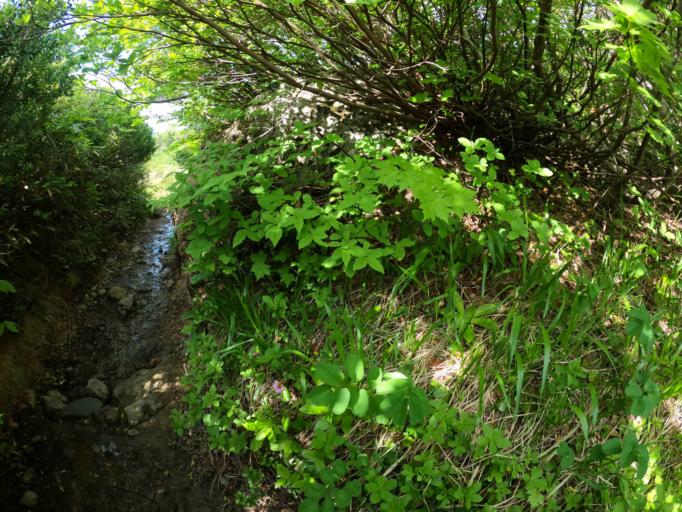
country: JP
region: Akita
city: Yuzawa
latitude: 38.9755
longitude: 140.7780
